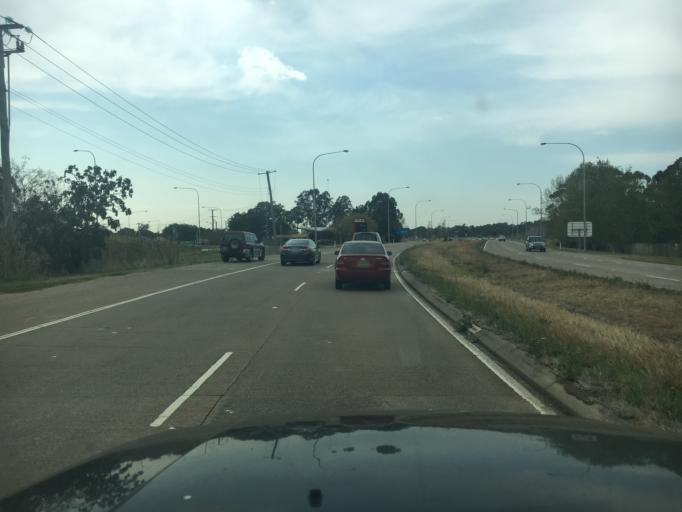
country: AU
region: New South Wales
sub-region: Maitland Municipality
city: Lorn
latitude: -32.7419
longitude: 151.5655
